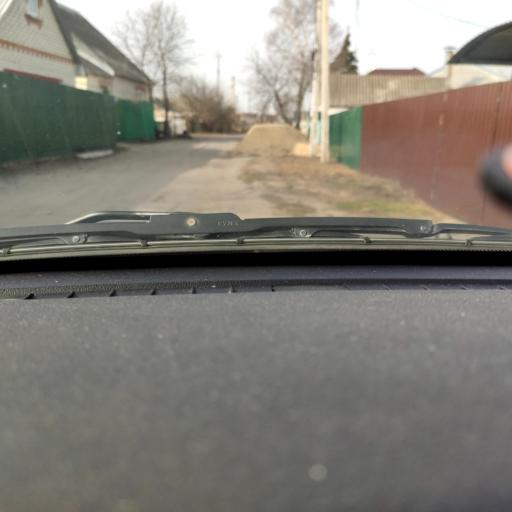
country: RU
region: Voronezj
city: Novaya Usman'
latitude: 51.6152
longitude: 39.3964
